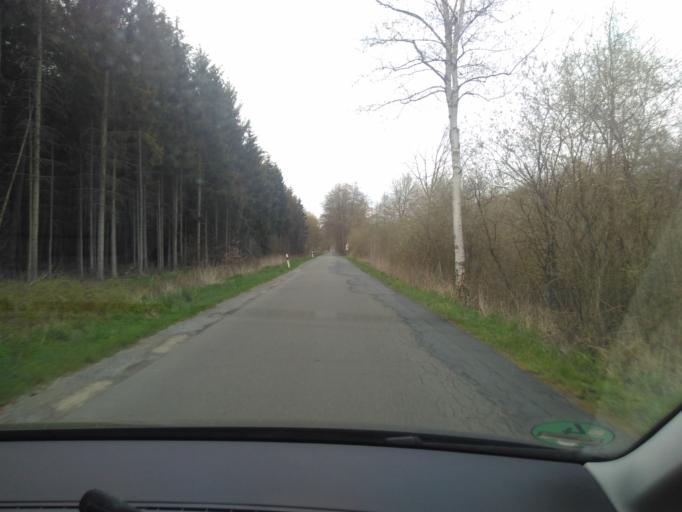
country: DE
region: Lower Saxony
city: Adelheidsdorf
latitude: 52.5331
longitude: 10.0325
